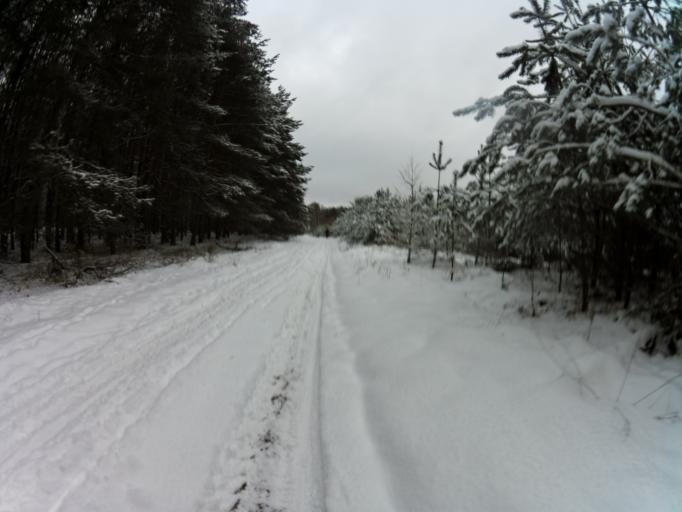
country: PL
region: West Pomeranian Voivodeship
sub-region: Powiat stargardzki
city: Dobrzany
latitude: 53.3574
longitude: 15.5145
